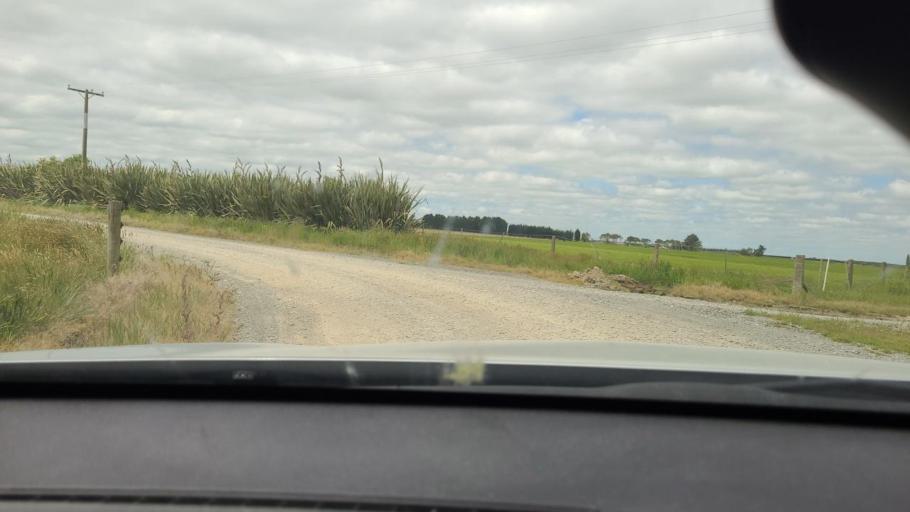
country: NZ
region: Southland
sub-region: Southland District
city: Winton
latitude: -46.2301
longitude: 168.2007
